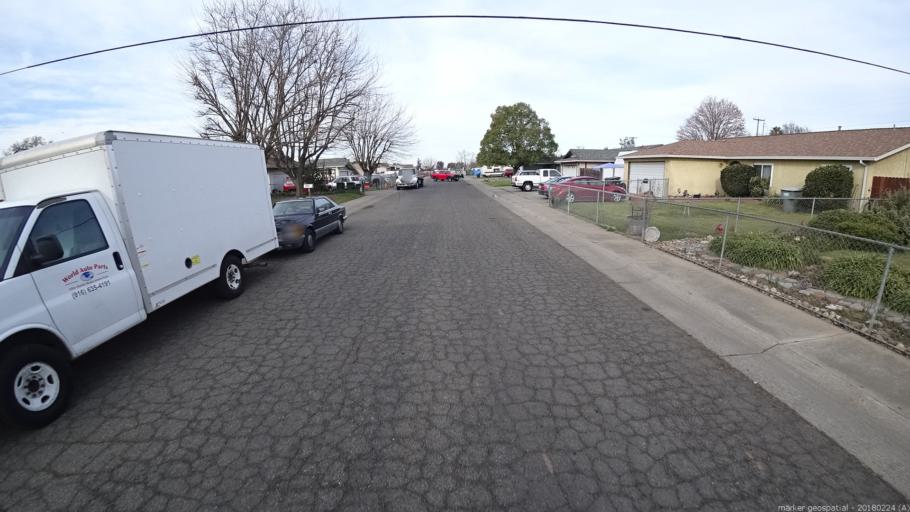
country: US
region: California
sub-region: Sacramento County
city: Rio Linda
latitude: 38.6782
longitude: -121.4684
